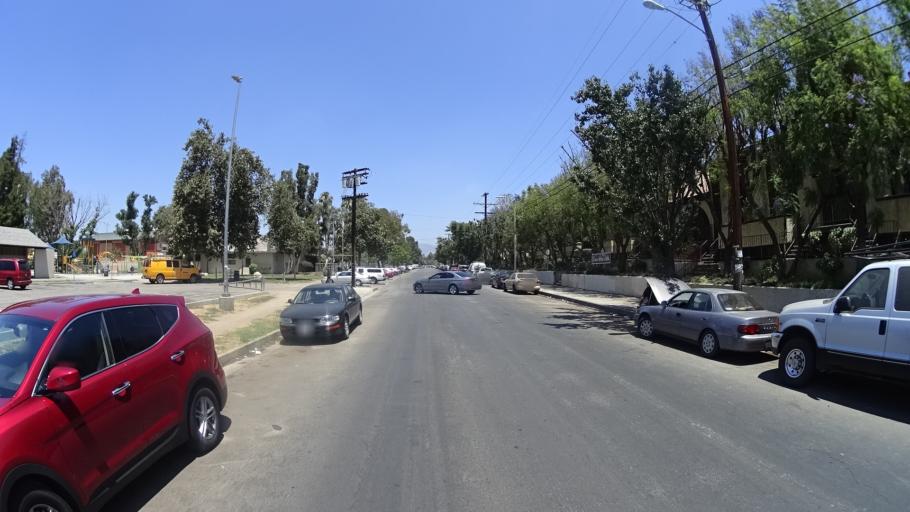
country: US
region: California
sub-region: Los Angeles County
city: Van Nuys
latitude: 34.2291
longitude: -118.4575
